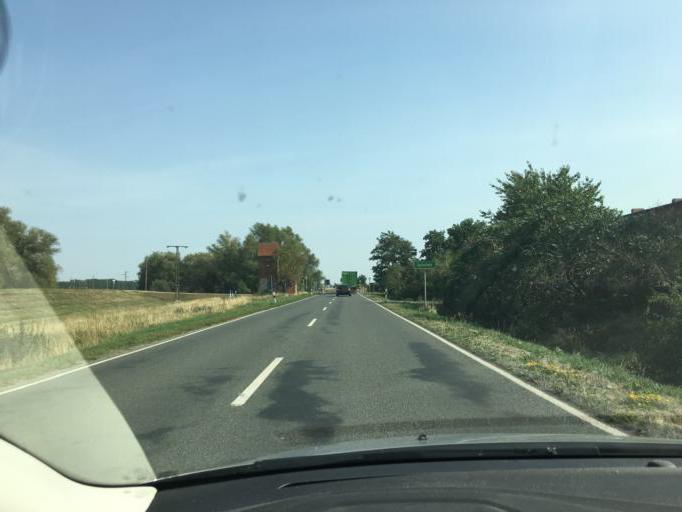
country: DE
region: Saxony-Anhalt
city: Plotzky
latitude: 52.0068
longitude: 11.7991
